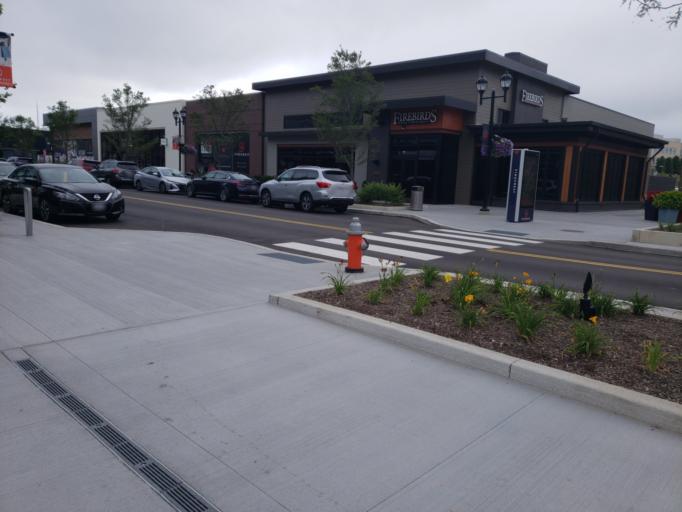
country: US
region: Ohio
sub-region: Cuyahoga County
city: Orange
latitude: 41.4542
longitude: -81.4862
